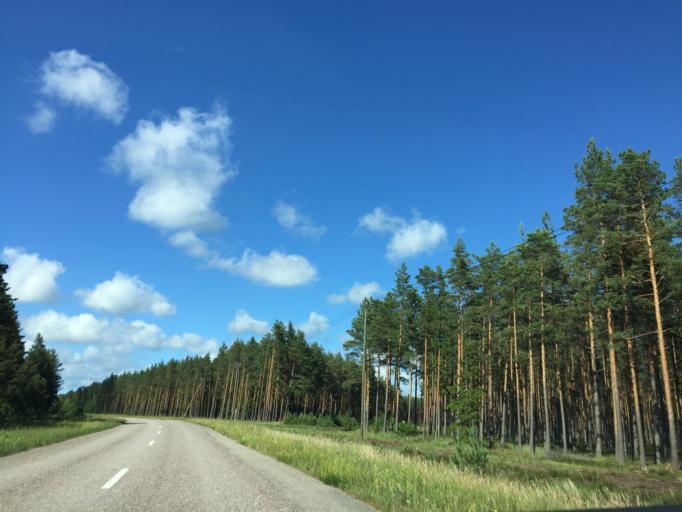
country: LV
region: Ventspils
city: Ventspils
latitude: 57.4983
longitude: 21.6881
